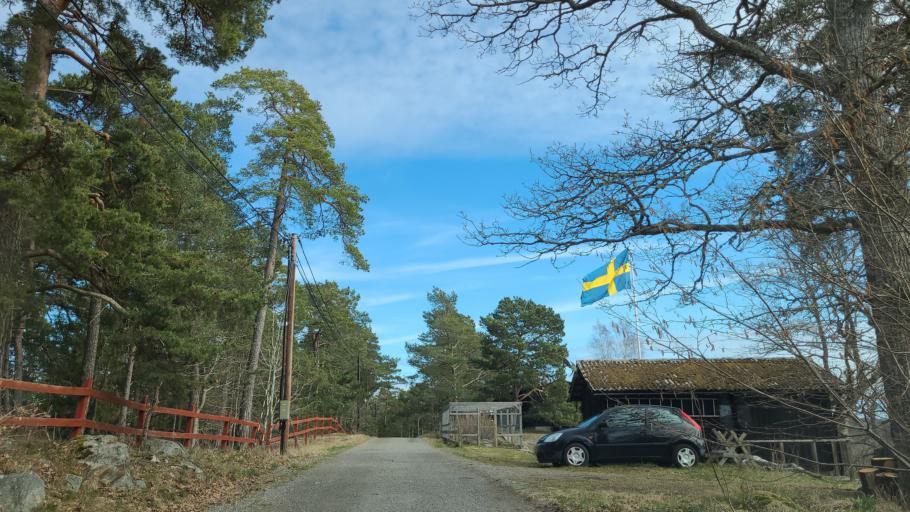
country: SE
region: Stockholm
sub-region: Varmdo Kommun
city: Hemmesta
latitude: 59.2793
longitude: 18.5373
